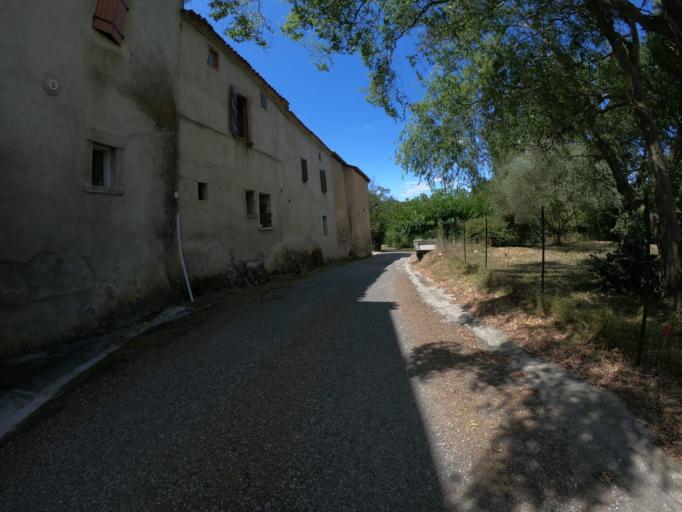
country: FR
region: Midi-Pyrenees
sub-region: Departement de l'Ariege
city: Verniolle
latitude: 43.0778
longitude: 1.7346
